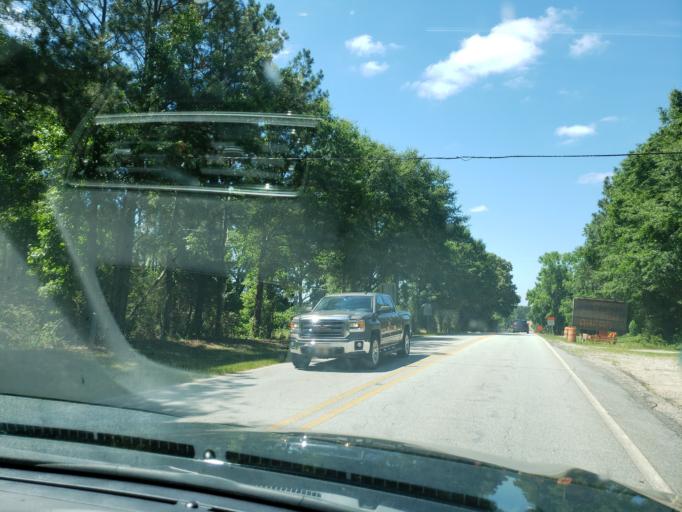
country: US
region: Alabama
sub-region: Lee County
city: Auburn
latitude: 32.6734
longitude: -85.4873
